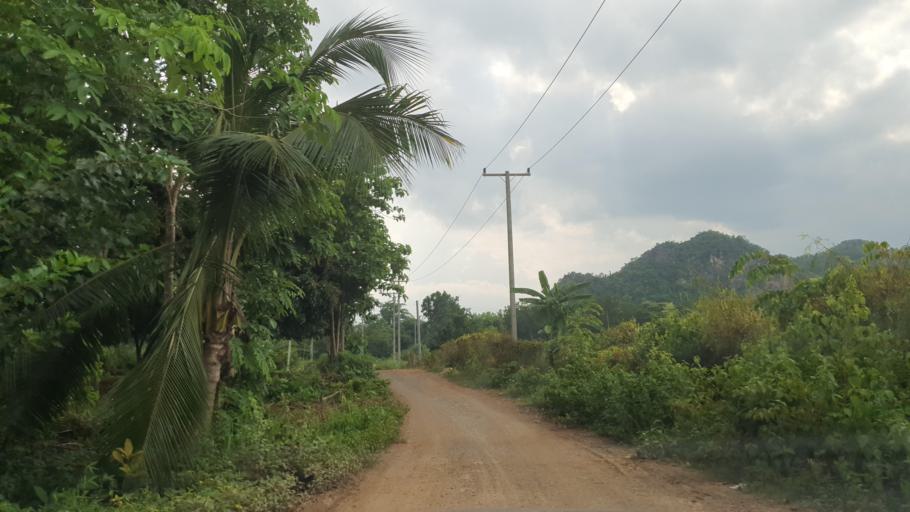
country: TH
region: Sukhothai
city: Thung Saliam
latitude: 17.2504
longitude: 99.5470
